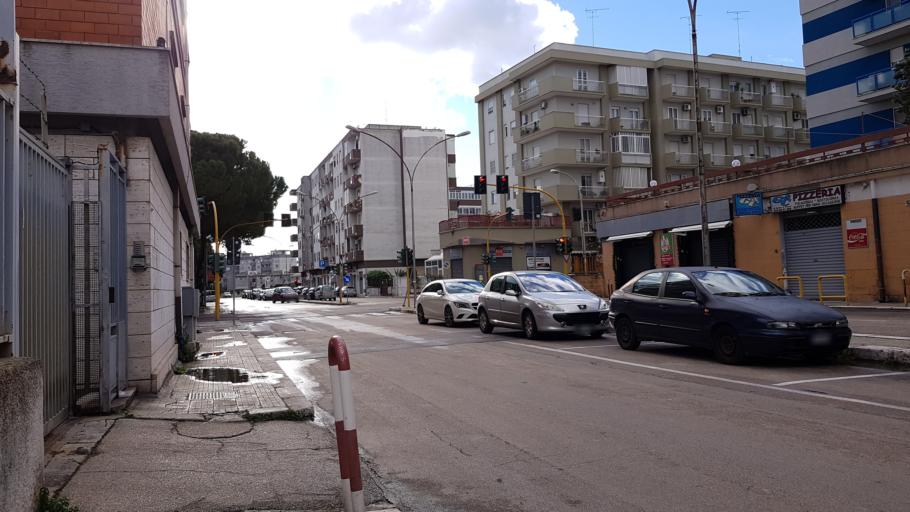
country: IT
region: Apulia
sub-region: Provincia di Brindisi
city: Brindisi
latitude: 40.6268
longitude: 17.9278
